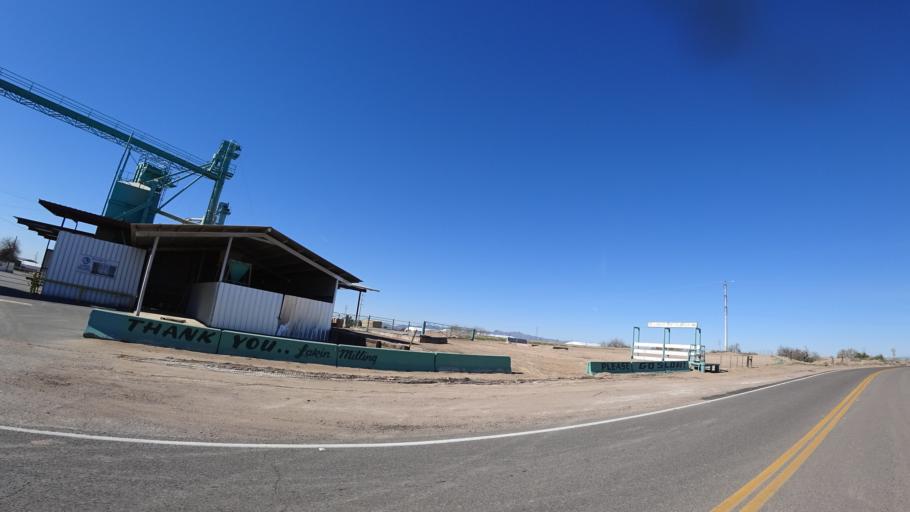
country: US
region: Arizona
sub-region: Maricopa County
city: Avondale
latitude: 33.4083
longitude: -112.3405
